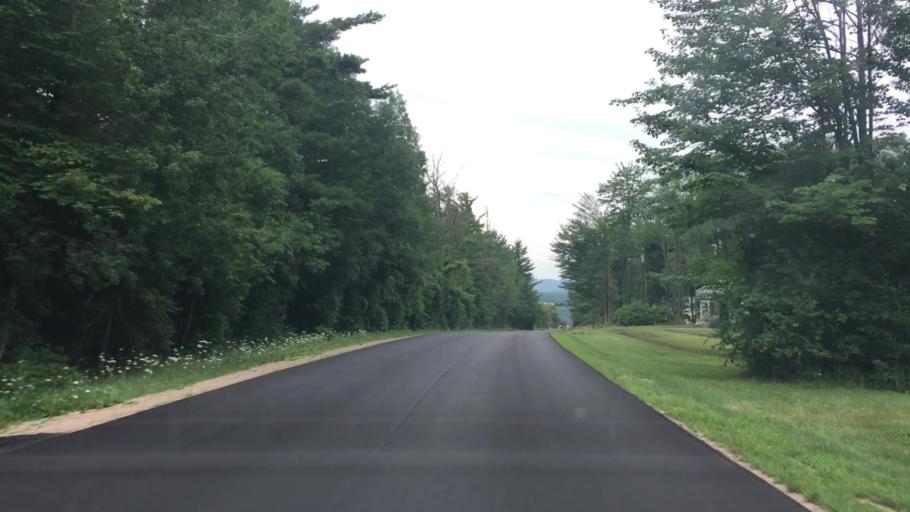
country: US
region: New York
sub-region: Clinton County
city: Peru
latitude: 44.5509
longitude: -73.5650
